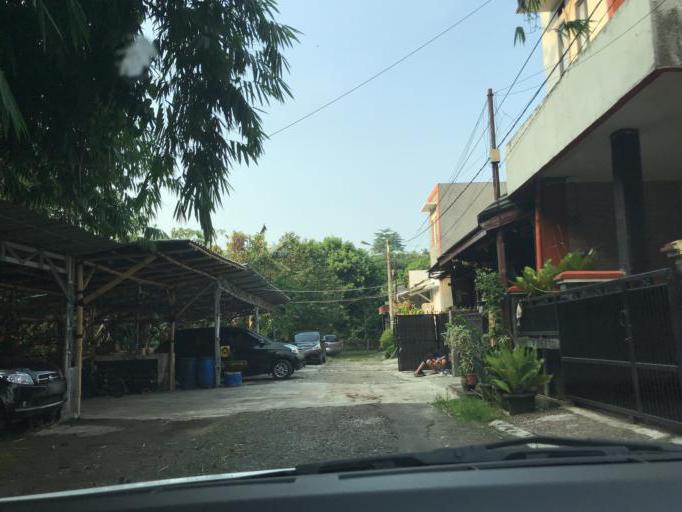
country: ID
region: West Java
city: Cibinong
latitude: -6.4727
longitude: 106.8183
